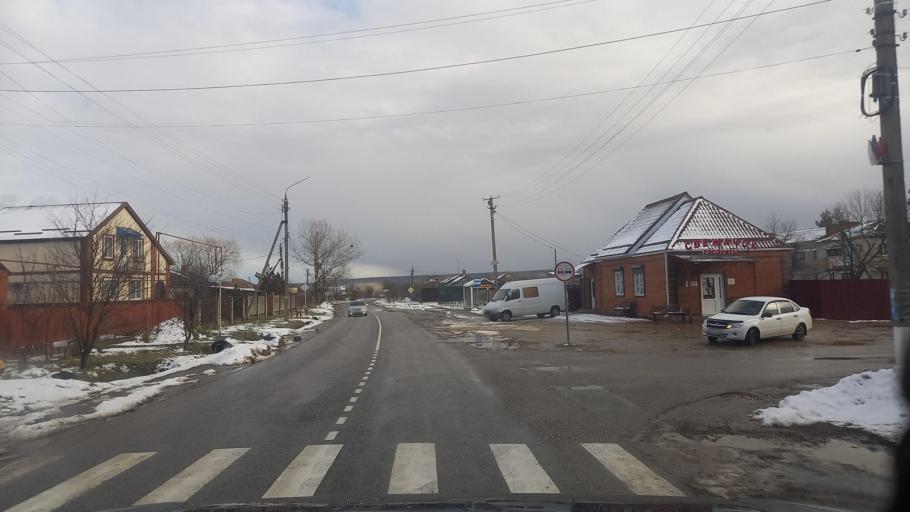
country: RU
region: Krasnodarskiy
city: Smolenskaya
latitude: 44.7764
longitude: 38.8378
